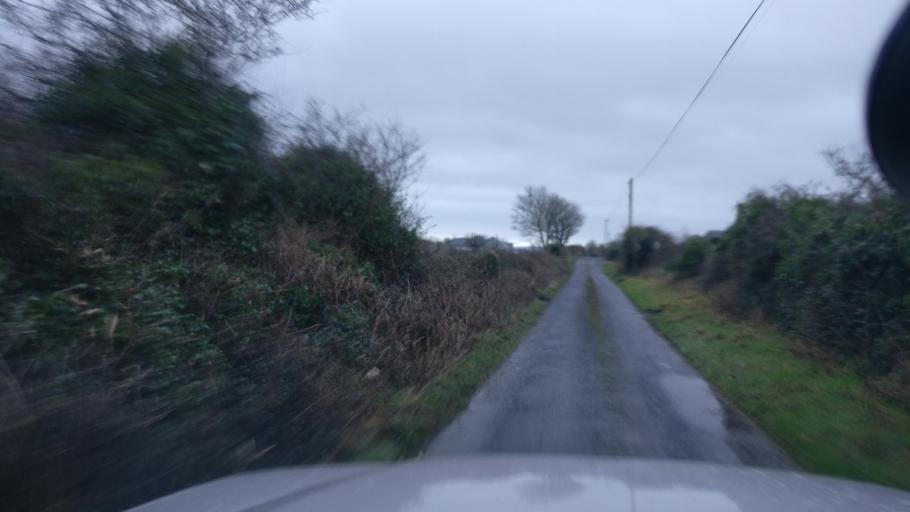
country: IE
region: Connaught
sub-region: County Galway
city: Loughrea
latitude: 53.2041
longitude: -8.6475
